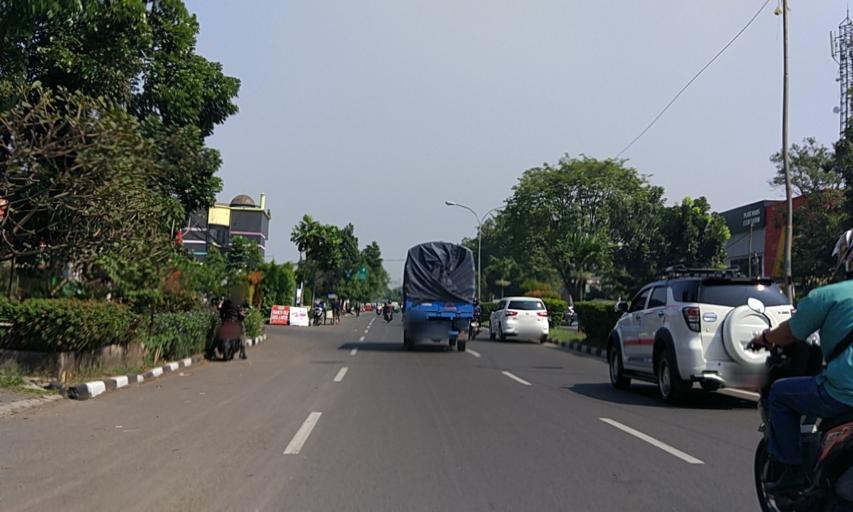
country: ID
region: West Java
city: Bandung
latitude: -6.9381
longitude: 107.6175
